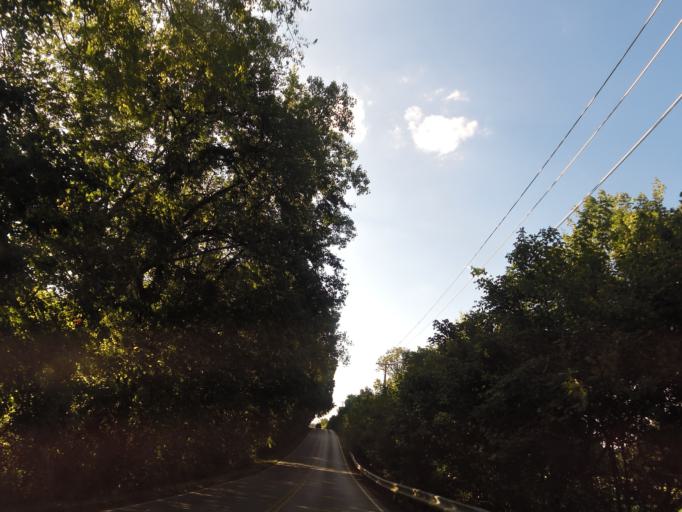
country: US
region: Tennessee
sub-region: Blount County
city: Eagleton Village
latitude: 35.8287
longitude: -83.9467
